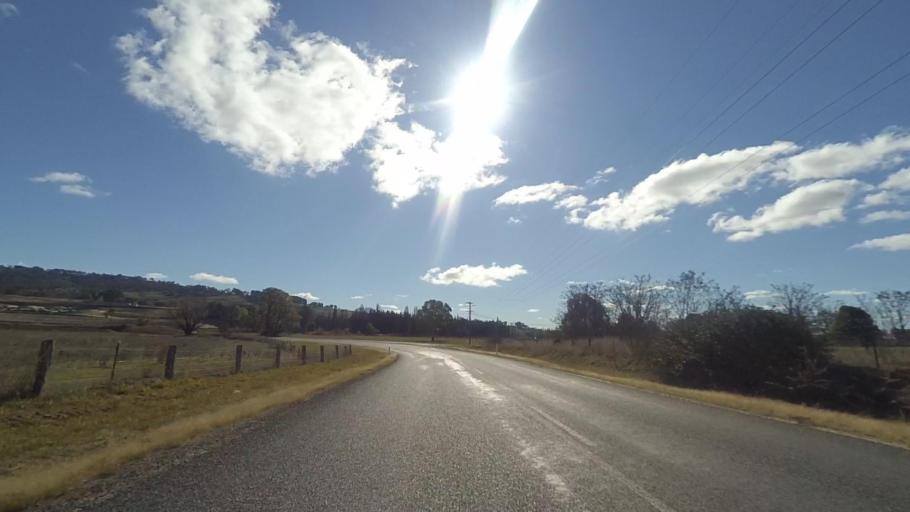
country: AU
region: New South Wales
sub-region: Bathurst Regional
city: Perthville
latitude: -33.4676
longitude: 149.5735
